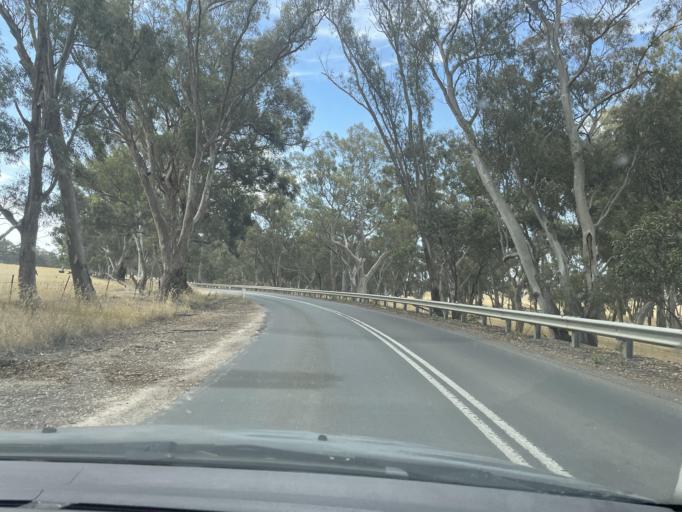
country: AU
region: South Australia
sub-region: Clare and Gilbert Valleys
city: Clare
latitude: -33.9007
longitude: 138.6439
